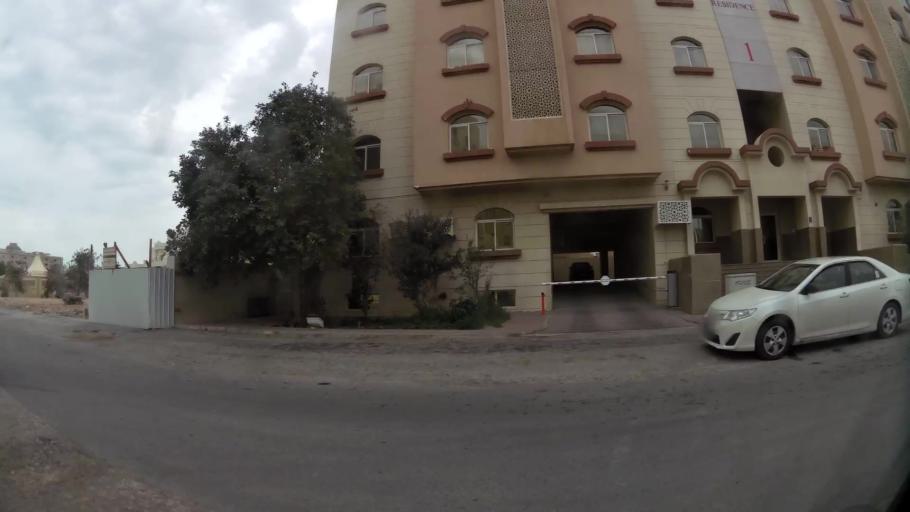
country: QA
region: Baladiyat ad Dawhah
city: Doha
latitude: 25.2793
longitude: 51.5005
